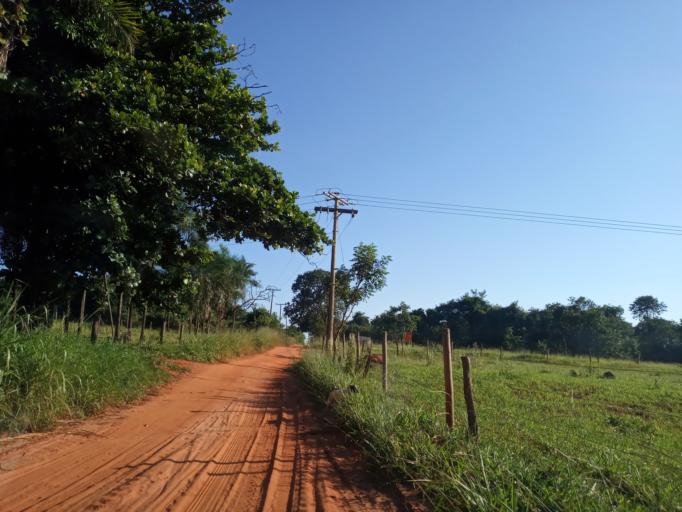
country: BR
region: Minas Gerais
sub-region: Ituiutaba
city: Ituiutaba
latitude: -18.9772
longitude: -49.5020
